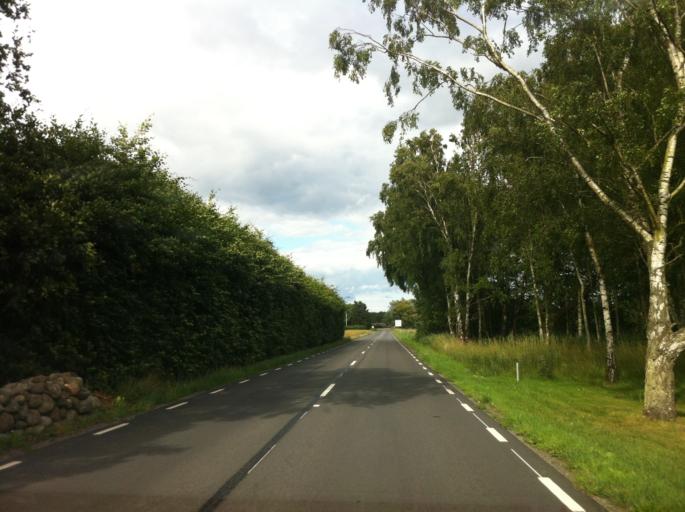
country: SE
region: Skane
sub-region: Simrishamns Kommun
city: Simrishamn
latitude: 55.3984
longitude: 14.1806
